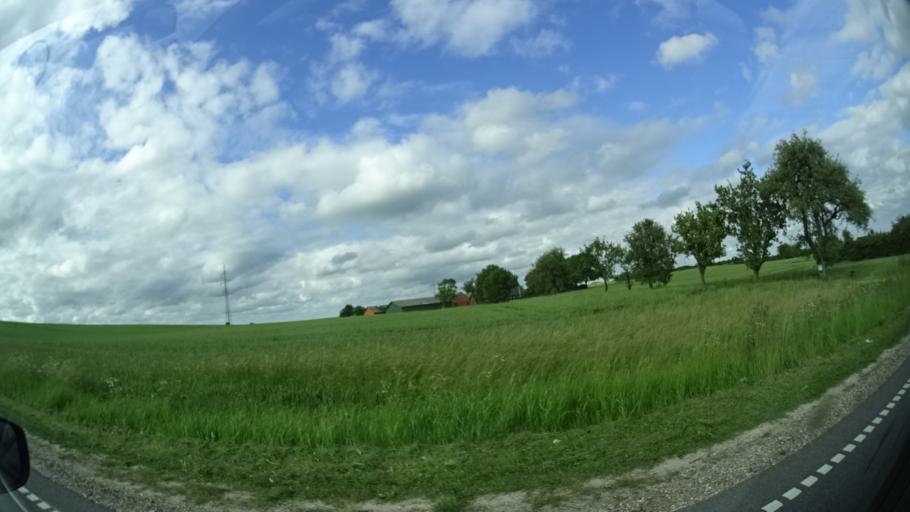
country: DK
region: Central Jutland
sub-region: Syddjurs Kommune
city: Ronde
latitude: 56.3174
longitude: 10.4220
